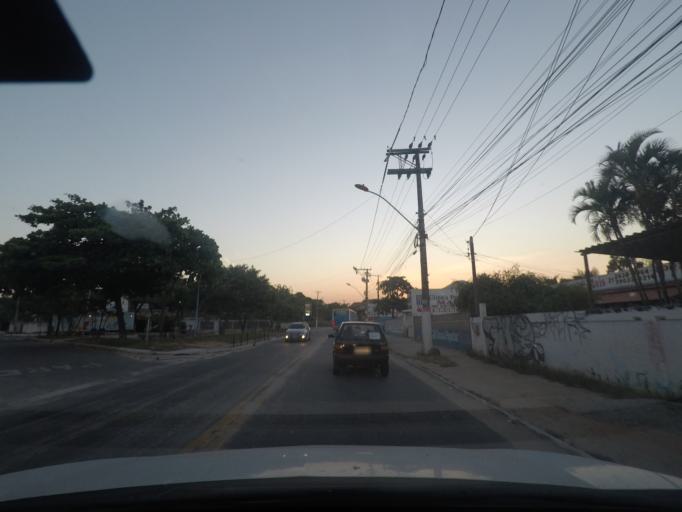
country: BR
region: Rio de Janeiro
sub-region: Niteroi
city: Niteroi
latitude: -22.9617
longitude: -42.9864
